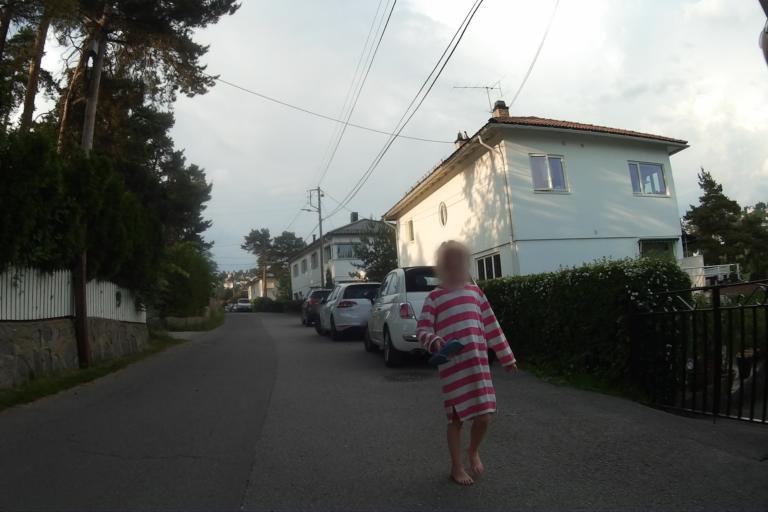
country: NO
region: Oslo
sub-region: Oslo
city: Oslo
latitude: 59.8672
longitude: 10.7734
